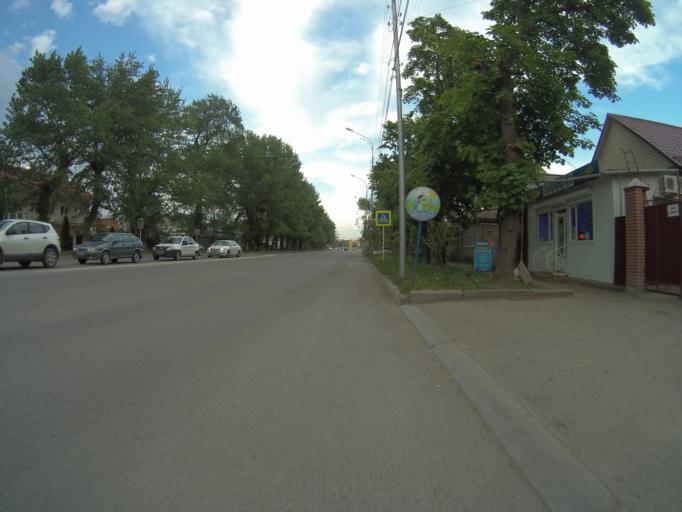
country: RU
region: Stavropol'skiy
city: Yessentuki
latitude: 44.0386
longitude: 42.8667
